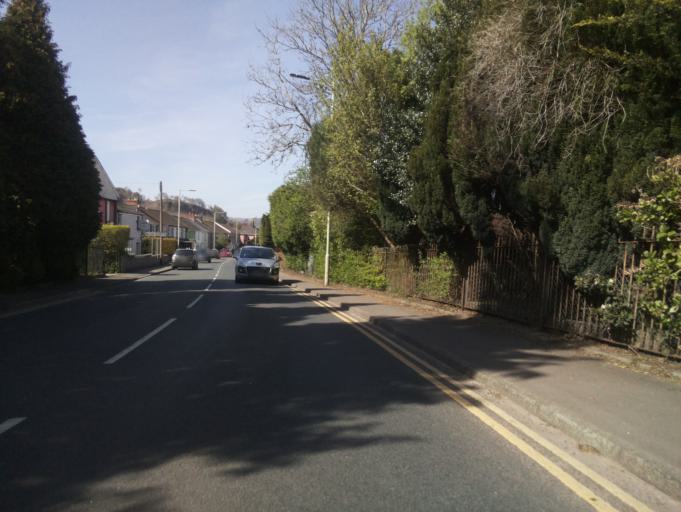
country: GB
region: Wales
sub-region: Cardiff
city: Pentyrch
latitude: 51.5475
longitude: -3.2710
